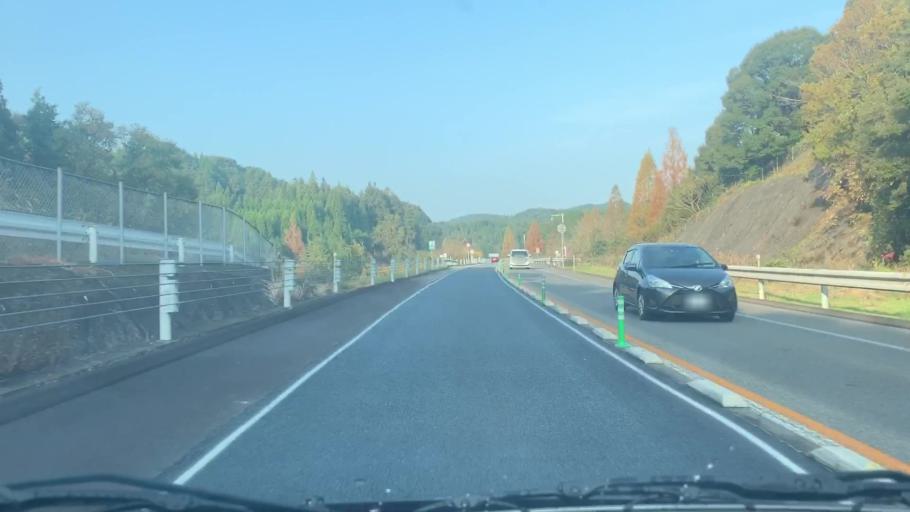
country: JP
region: Saga Prefecture
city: Ureshinomachi-shimojuku
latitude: 33.1434
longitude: 129.9720
